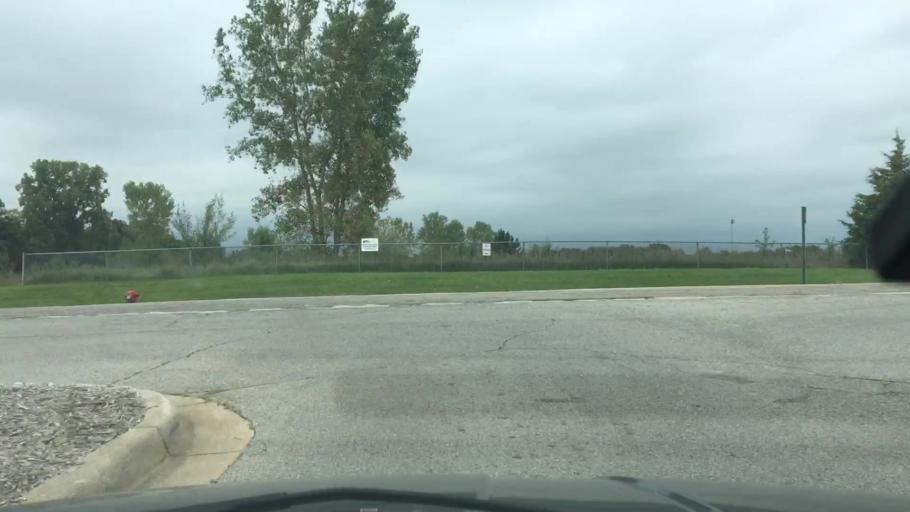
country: US
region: Michigan
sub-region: Livingston County
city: Brighton
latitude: 42.5075
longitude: -83.7838
